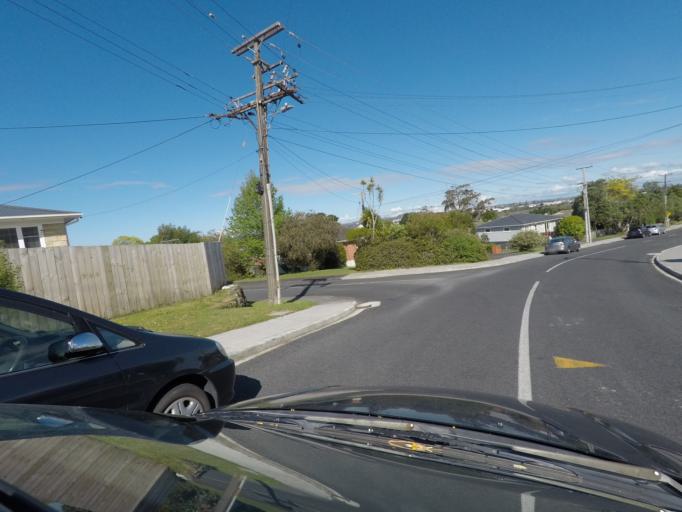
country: NZ
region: Auckland
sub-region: Auckland
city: Rosebank
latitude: -36.8626
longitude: 174.6518
